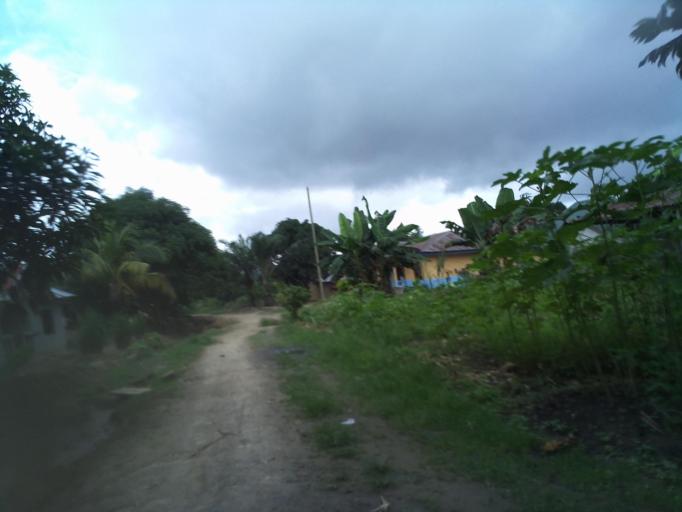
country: SL
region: Eastern Province
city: Kenema
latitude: 7.8327
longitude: -11.1829
